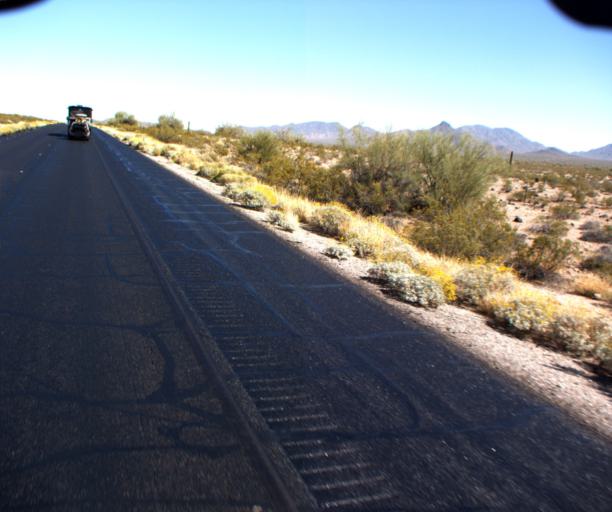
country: US
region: Arizona
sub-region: Pinal County
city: Maricopa
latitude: 32.8389
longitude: -112.2301
